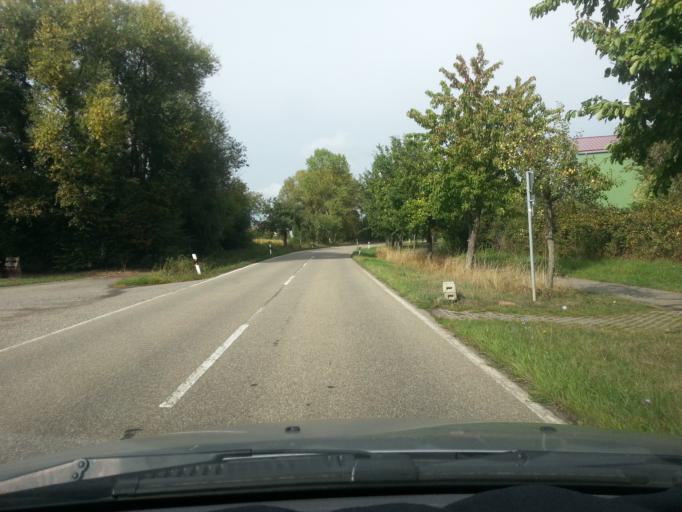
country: DE
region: Rheinland-Pfalz
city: Venningen
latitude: 49.2773
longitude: 8.1731
